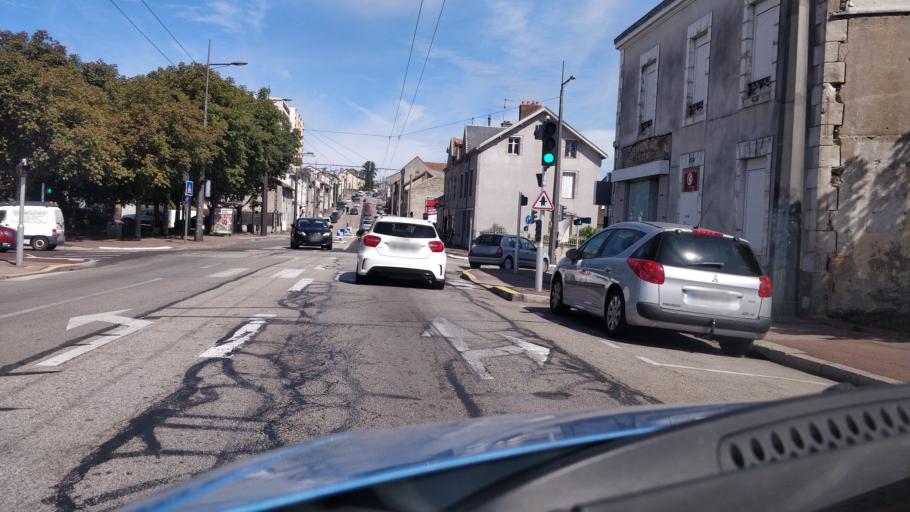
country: FR
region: Limousin
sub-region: Departement de la Haute-Vienne
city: Limoges
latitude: 45.8482
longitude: 1.2621
